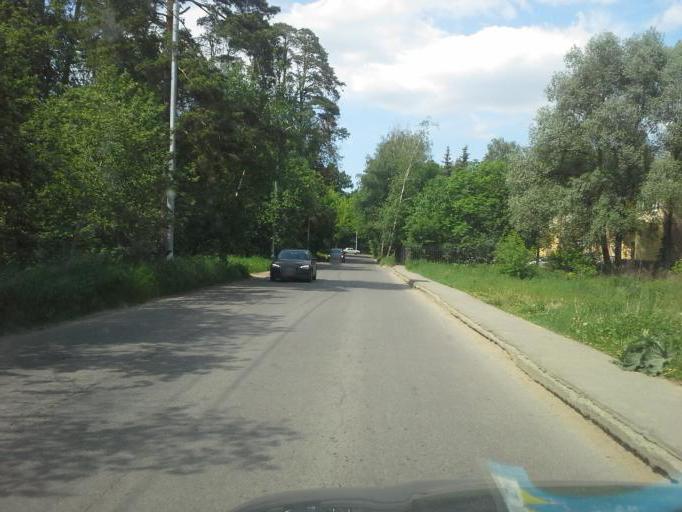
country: RU
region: Moskovskaya
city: Barvikha
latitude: 55.7208
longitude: 37.2741
